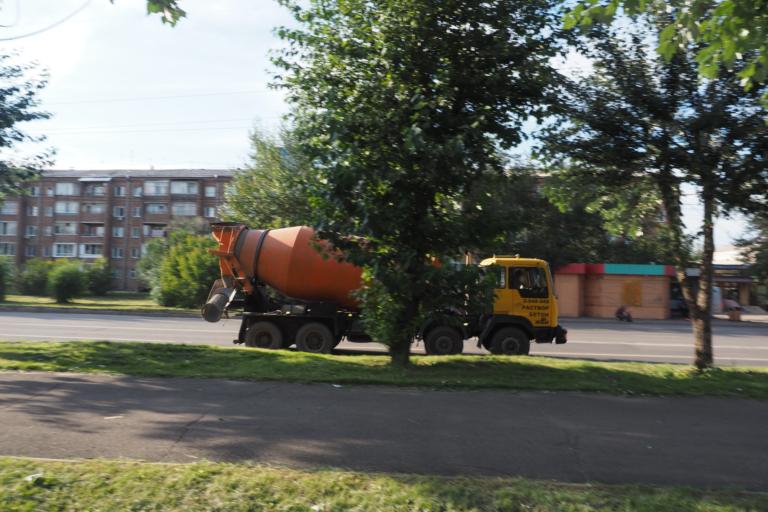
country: RU
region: Krasnoyarskiy
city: Berezovka
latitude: 55.9983
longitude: 93.0247
